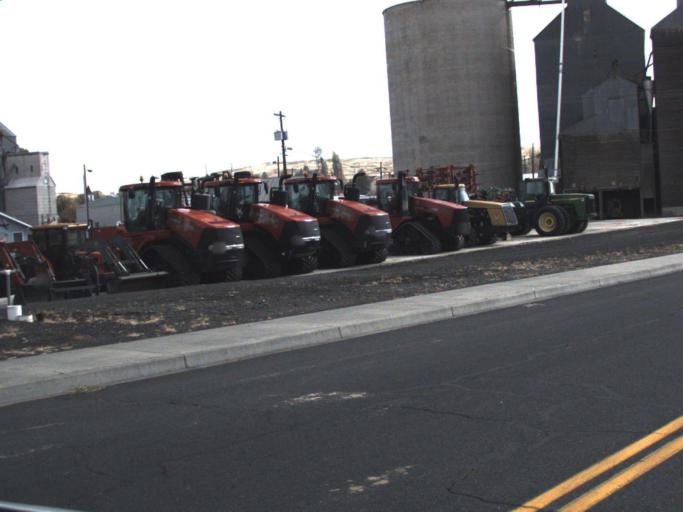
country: US
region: Washington
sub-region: Adams County
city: Ritzville
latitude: 47.3357
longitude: -118.6920
